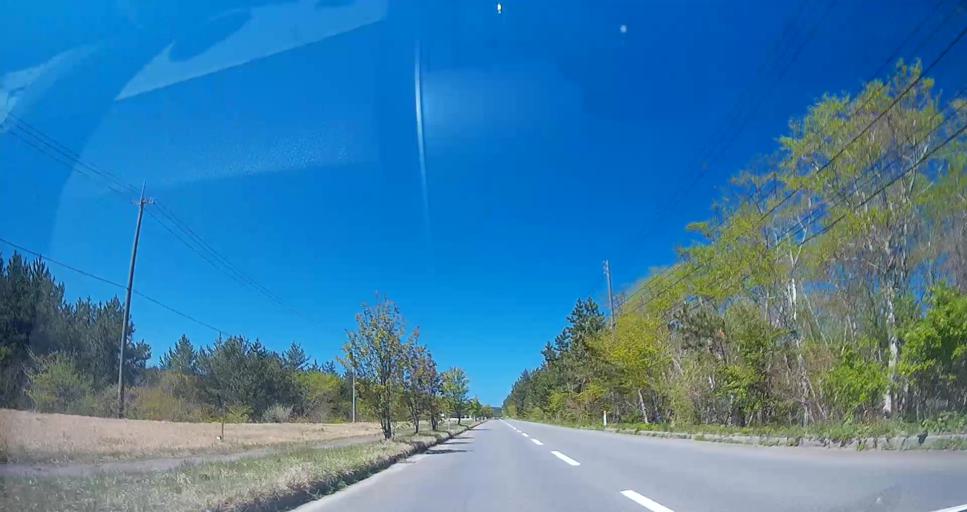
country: JP
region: Aomori
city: Misawa
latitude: 40.9439
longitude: 141.3674
